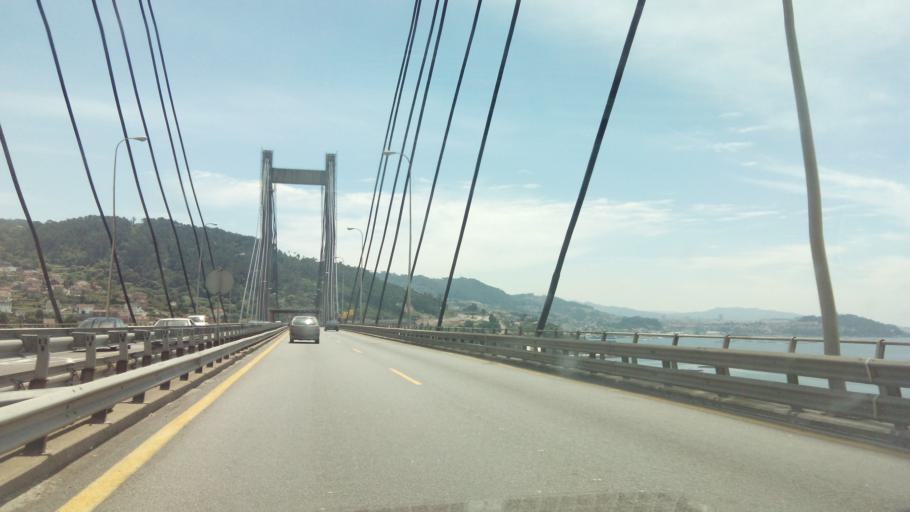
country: ES
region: Galicia
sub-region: Provincia de Pontevedra
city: Redondela
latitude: 42.2898
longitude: -8.6603
